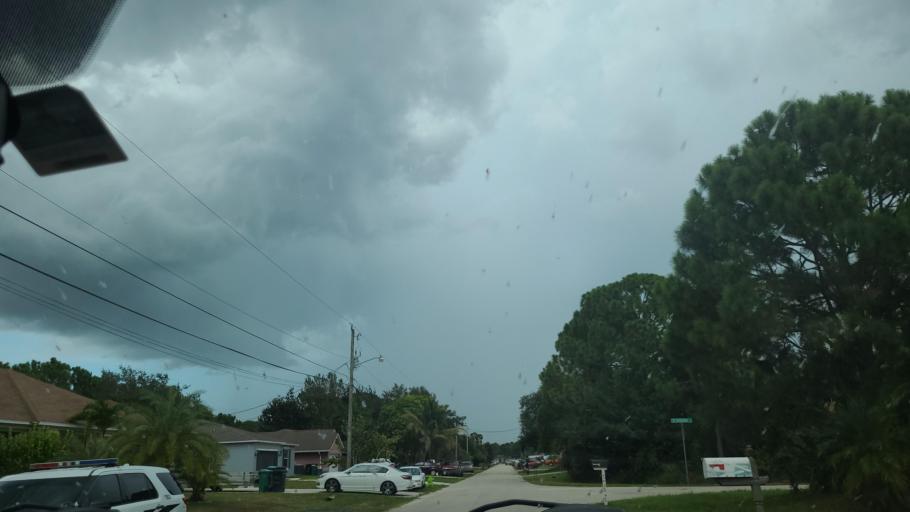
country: US
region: Florida
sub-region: Saint Lucie County
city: Port Saint Lucie
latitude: 27.2530
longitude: -80.4075
